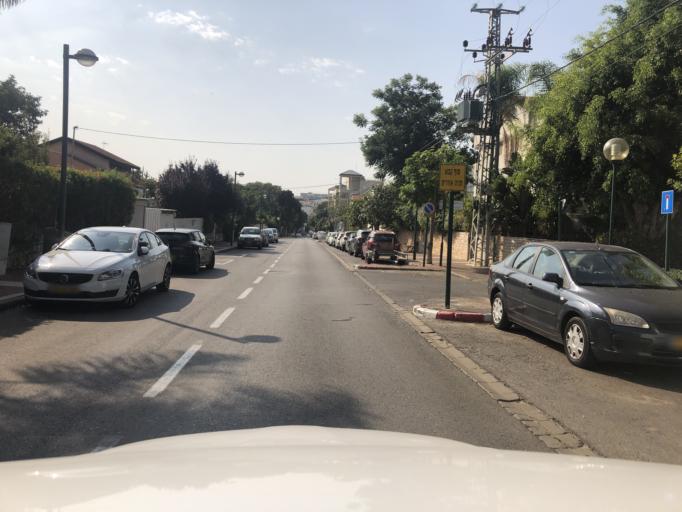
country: IL
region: Central District
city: Kfar Saba
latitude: 32.1824
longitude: 34.9072
